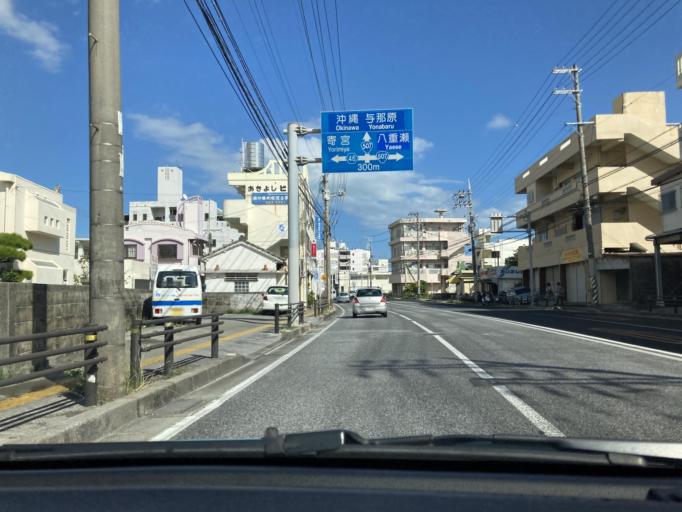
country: JP
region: Okinawa
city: Tomigusuku
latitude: 26.1958
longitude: 127.7013
